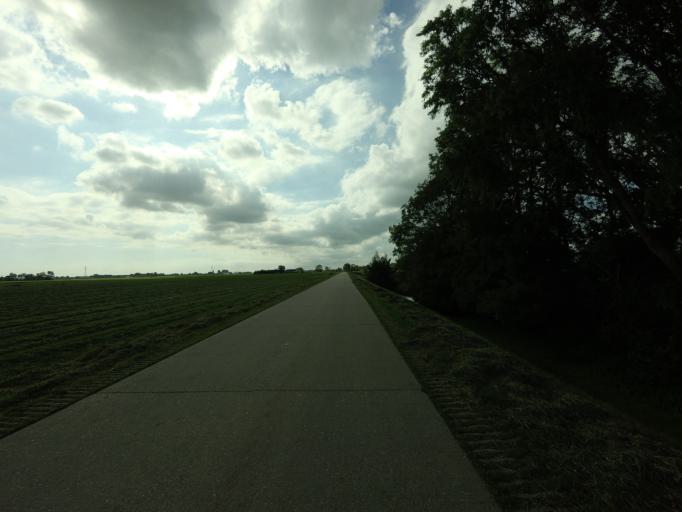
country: NL
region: Friesland
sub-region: Gemeente Littenseradiel
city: Wommels
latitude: 53.0730
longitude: 5.6042
